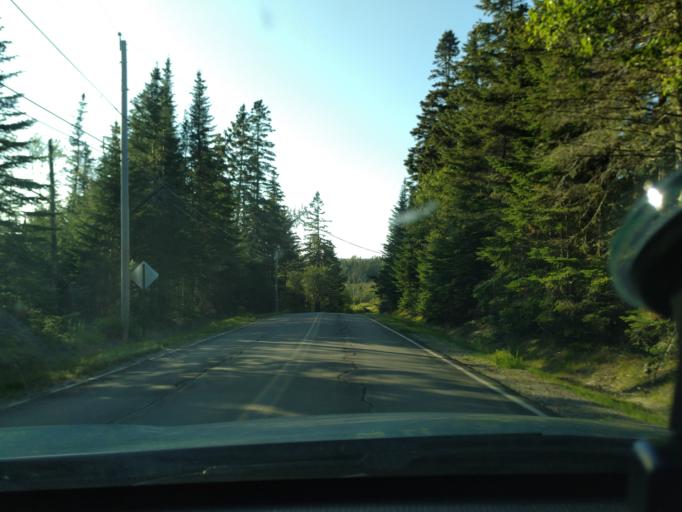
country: US
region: Maine
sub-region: Washington County
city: Machiasport
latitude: 44.6632
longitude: -67.2371
